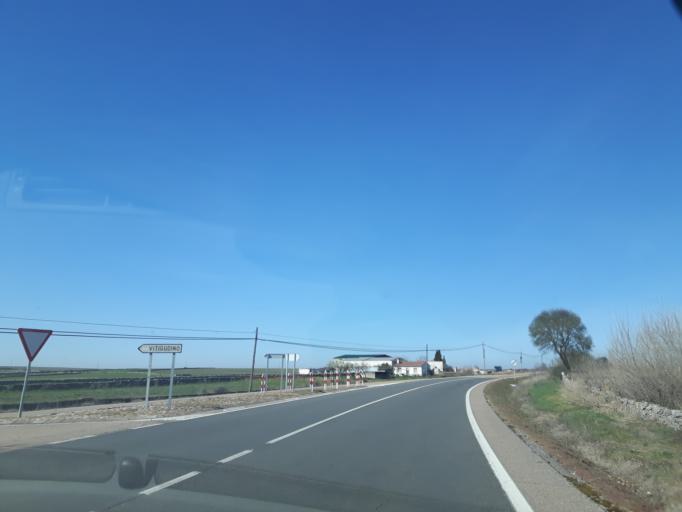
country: ES
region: Castille and Leon
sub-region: Provincia de Salamanca
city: Vitigudino
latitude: 41.0094
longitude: -6.4437
